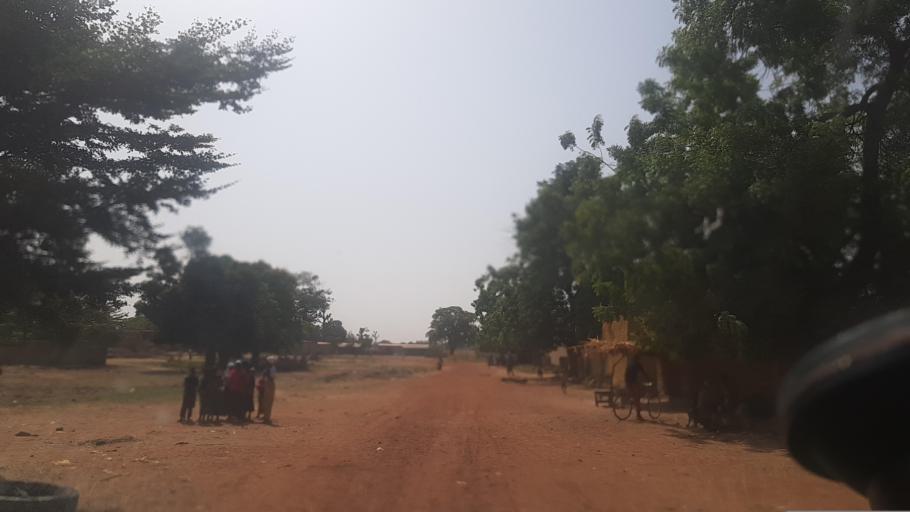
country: ML
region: Segou
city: Baroueli
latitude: 13.0113
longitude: -6.4225
